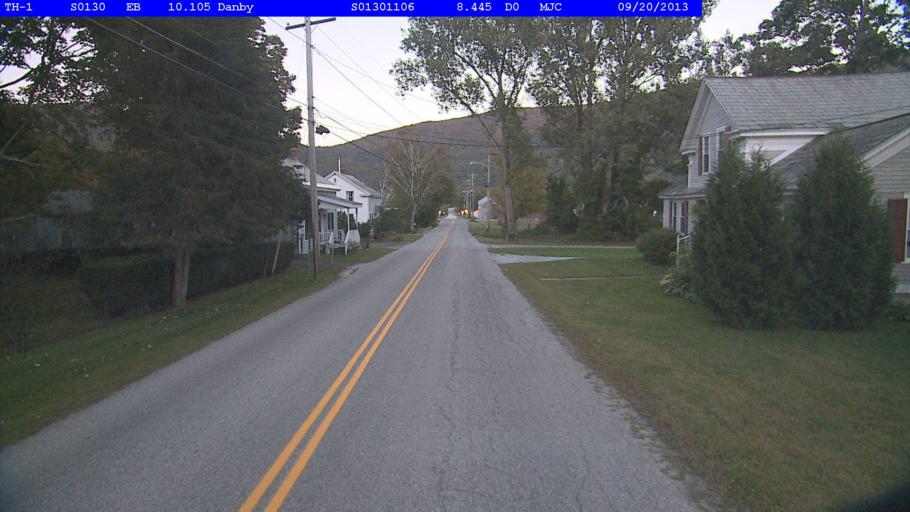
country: US
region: Vermont
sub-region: Bennington County
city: Manchester Center
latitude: 43.3467
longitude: -72.9946
